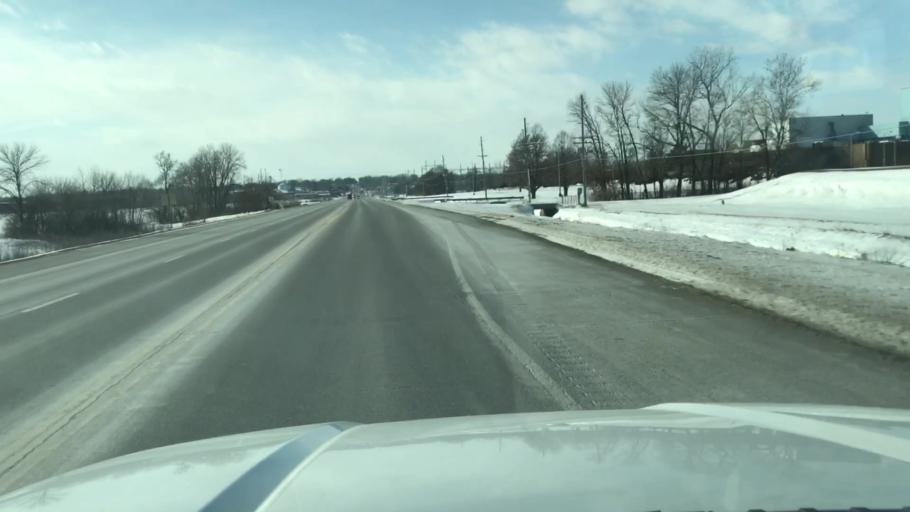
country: US
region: Missouri
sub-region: Nodaway County
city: Maryville
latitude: 40.3450
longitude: -94.8362
